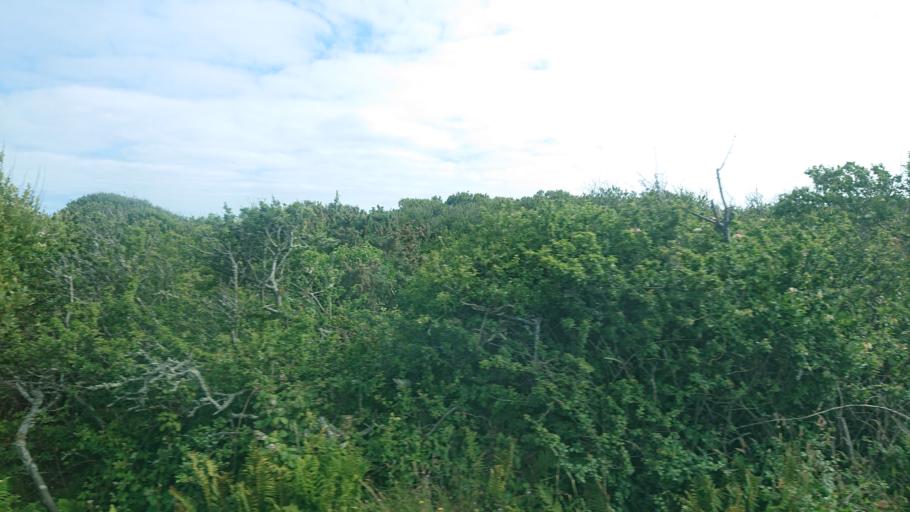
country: FR
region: Brittany
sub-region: Departement du Finistere
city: Porspoder
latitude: 48.4671
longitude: -5.0685
